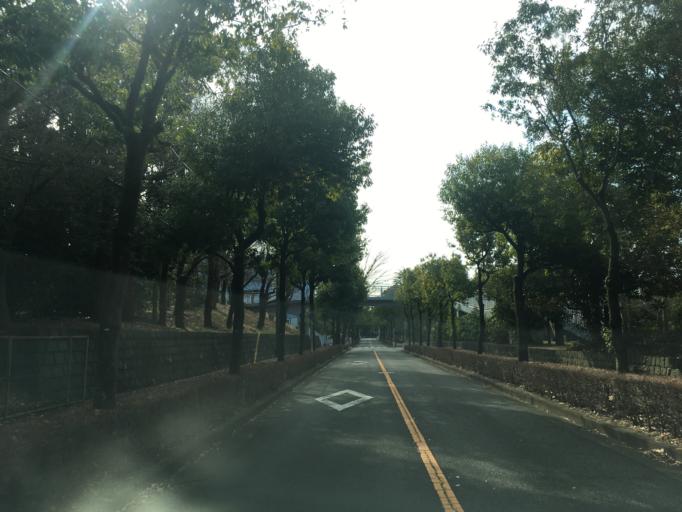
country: JP
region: Tokyo
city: Hino
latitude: 35.6162
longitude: 139.4346
